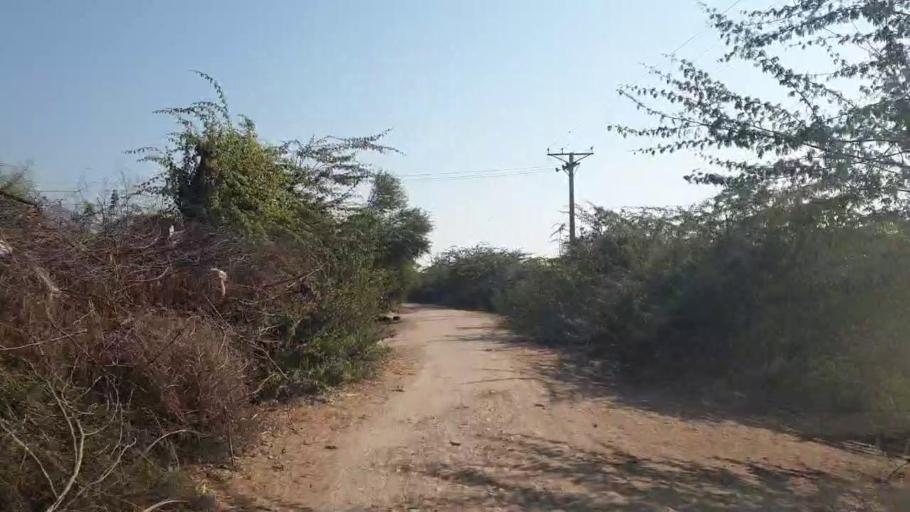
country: PK
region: Sindh
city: Shahpur Chakar
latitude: 26.0827
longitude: 68.5965
